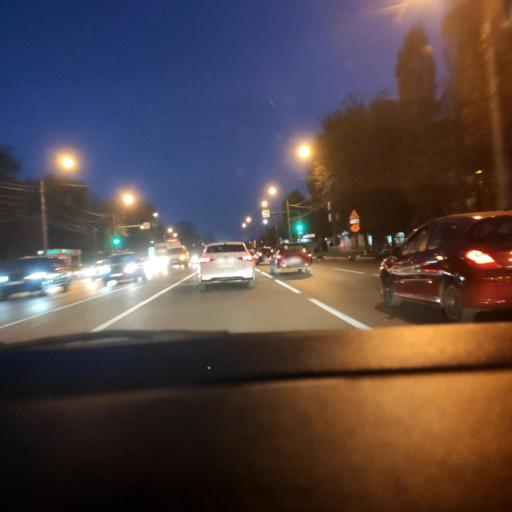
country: RU
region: Voronezj
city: Voronezh
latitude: 51.6698
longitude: 39.1637
